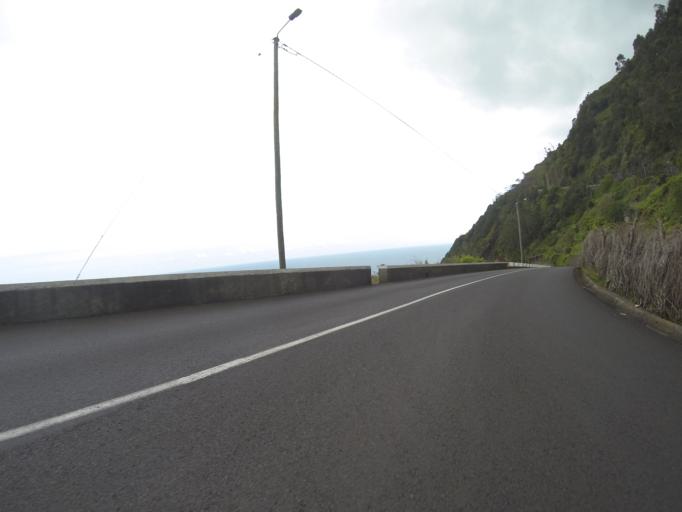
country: PT
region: Madeira
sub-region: Porto Moniz
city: Porto Moniz
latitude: 32.8629
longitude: -17.1751
